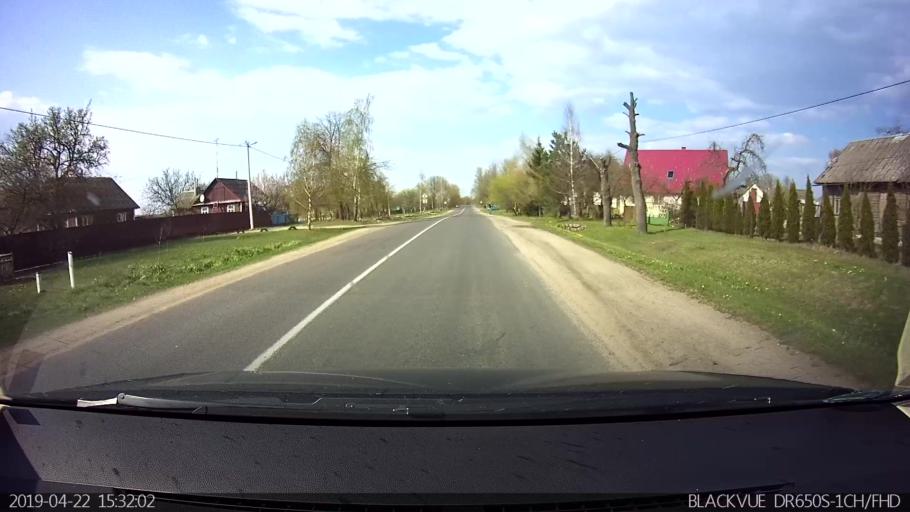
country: BY
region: Brest
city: Vysokaye
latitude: 52.4039
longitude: 23.3829
